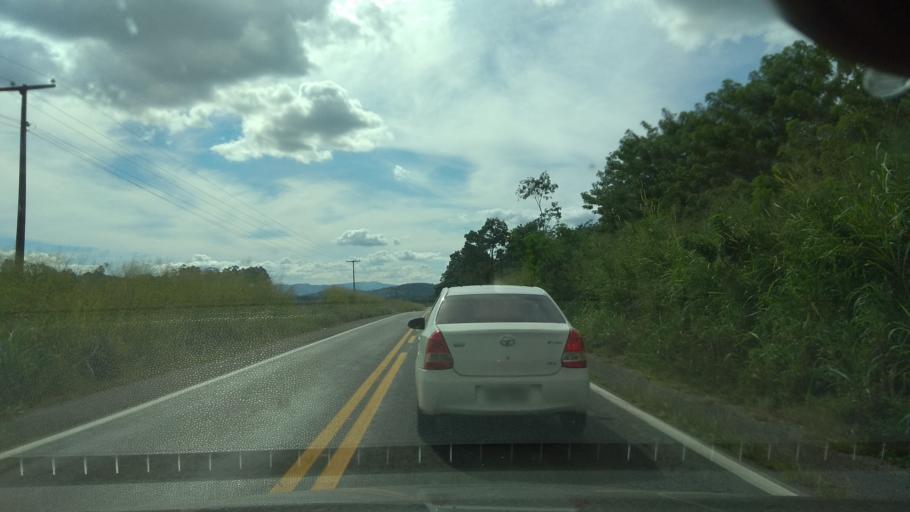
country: BR
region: Bahia
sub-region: Ipiau
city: Ipiau
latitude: -14.0782
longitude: -39.7825
